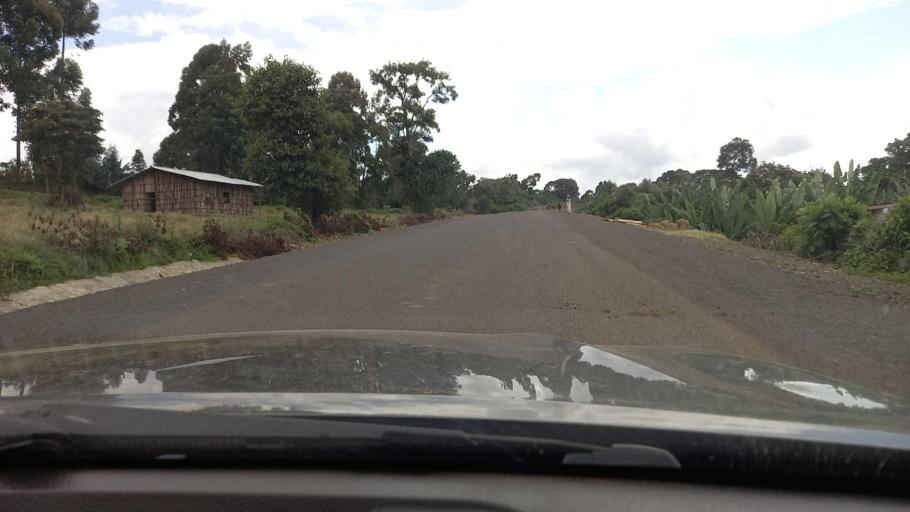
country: ET
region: Southern Nations, Nationalities, and People's Region
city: Mizan Teferi
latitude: 6.2101
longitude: 35.6135
